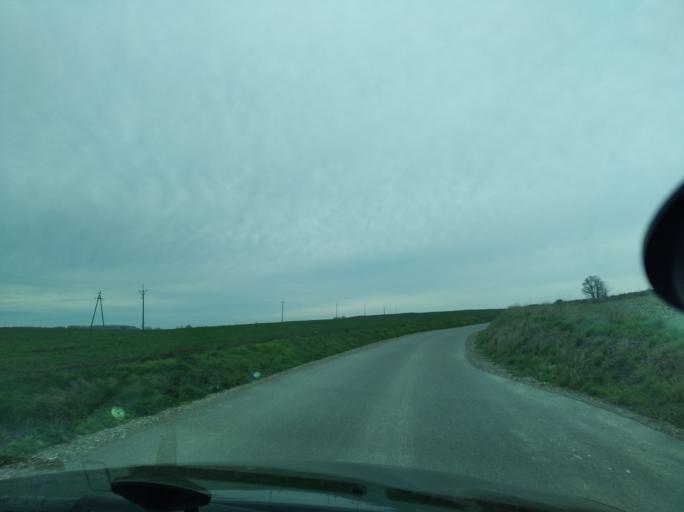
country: PL
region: Subcarpathian Voivodeship
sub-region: Powiat przeworski
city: Grzeska
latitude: 50.0659
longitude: 22.4657
